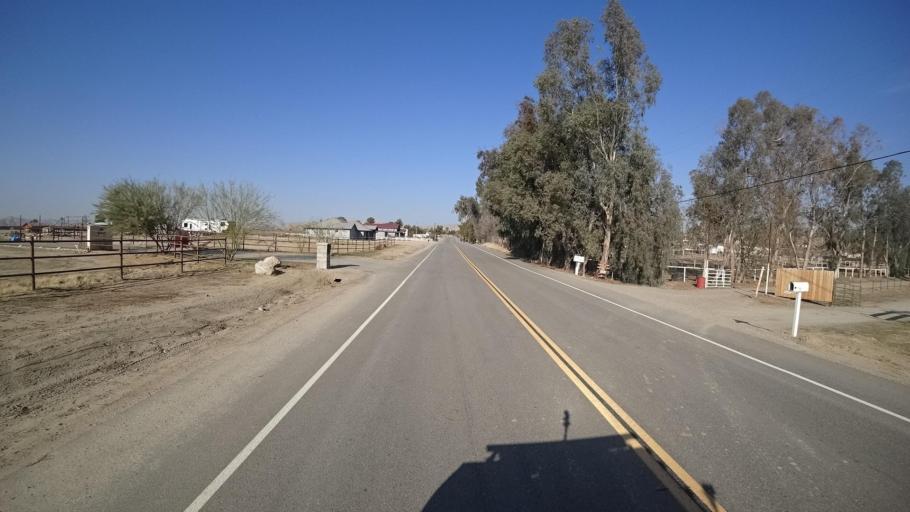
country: US
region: California
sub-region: Kern County
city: Oildale
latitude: 35.4384
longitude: -118.8911
